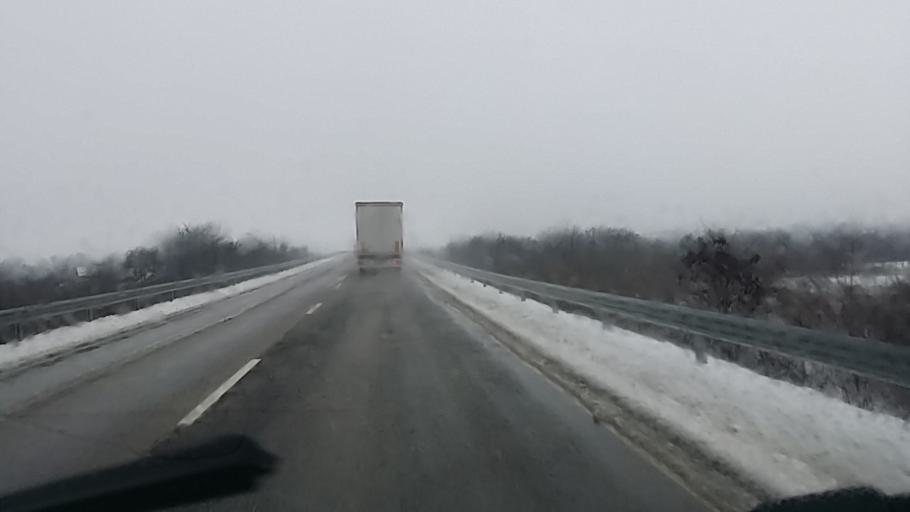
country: HU
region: Komarom-Esztergom
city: Komarom
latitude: 47.7396
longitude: 18.0938
